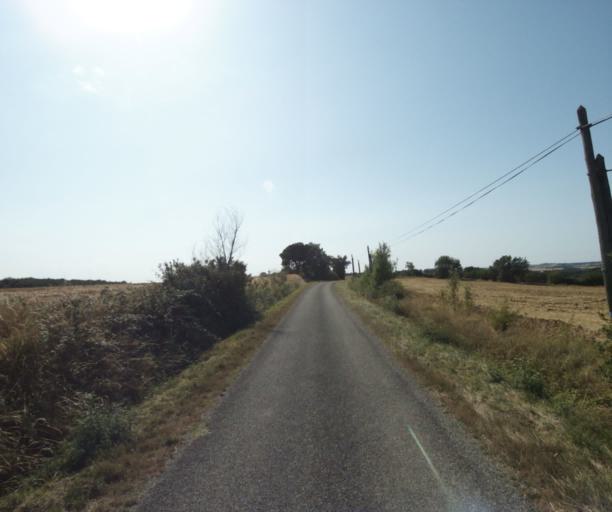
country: FR
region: Midi-Pyrenees
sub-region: Departement de la Haute-Garonne
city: Saint-Felix-Lauragais
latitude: 43.4243
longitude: 1.8367
